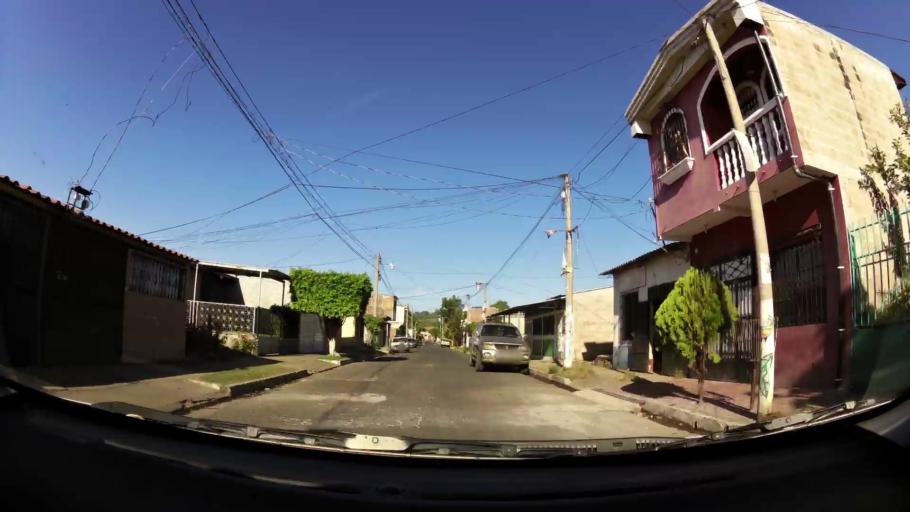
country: SV
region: Sonsonate
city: Sonzacate
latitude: 13.7299
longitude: -89.7107
